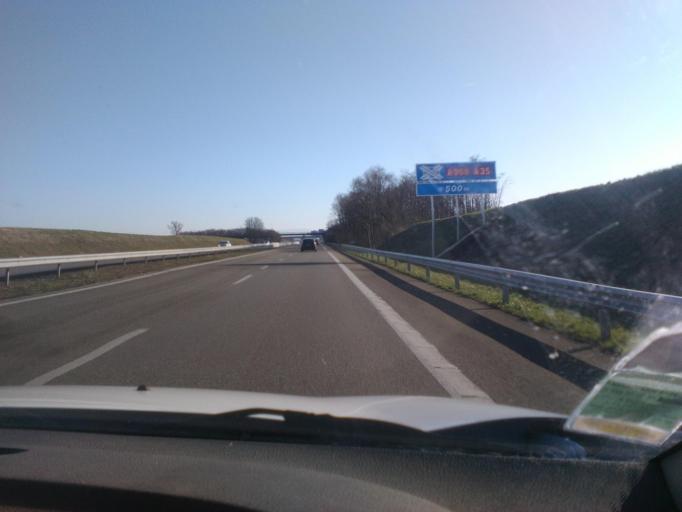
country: FR
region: Alsace
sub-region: Departement du Bas-Rhin
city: Duttlenheim
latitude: 48.5161
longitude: 7.5697
